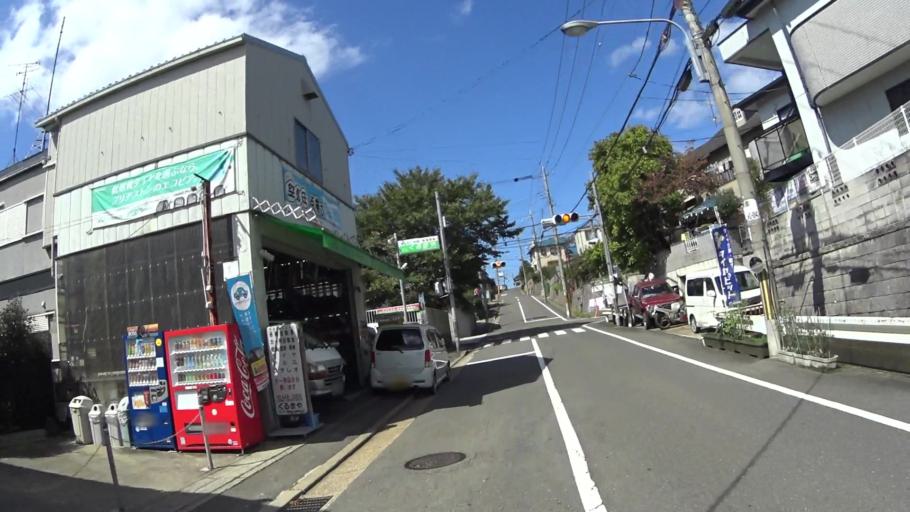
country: JP
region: Kyoto
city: Uji
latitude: 34.9415
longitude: 135.7855
